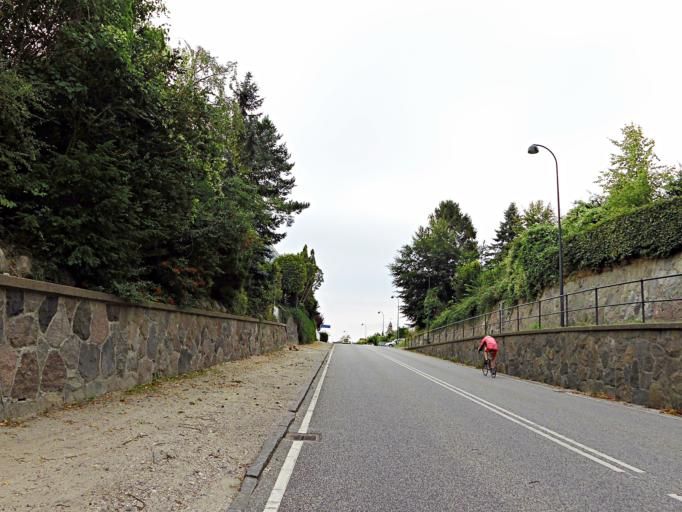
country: DK
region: Capital Region
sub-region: Rudersdal Kommune
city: Trorod
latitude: 55.8169
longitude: 12.5748
